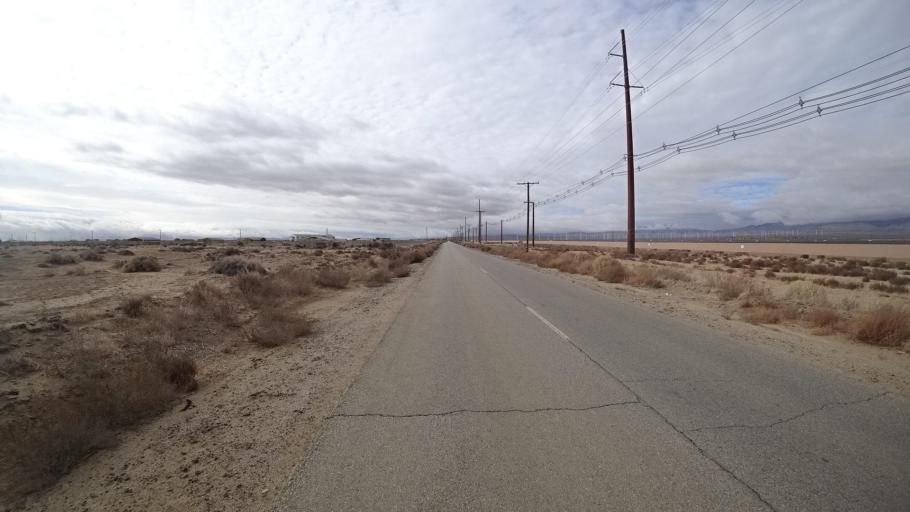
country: US
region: California
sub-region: Kern County
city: Rosamond
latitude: 34.8630
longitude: -118.3593
